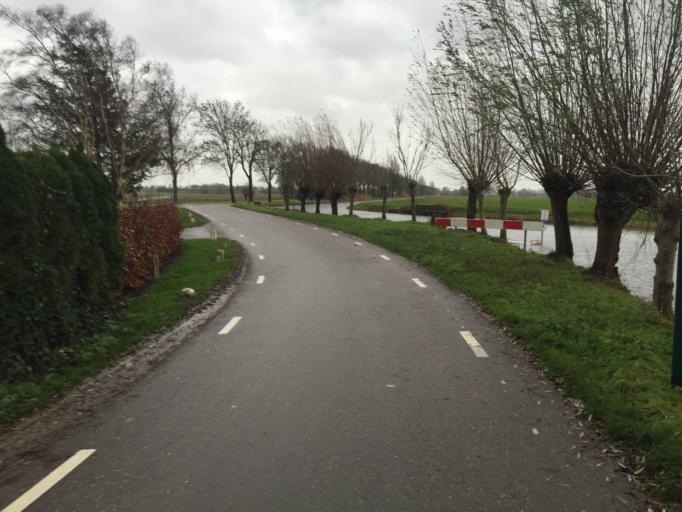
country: NL
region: Utrecht
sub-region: Gemeente Montfoort
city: Montfoort
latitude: 52.0601
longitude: 4.9405
